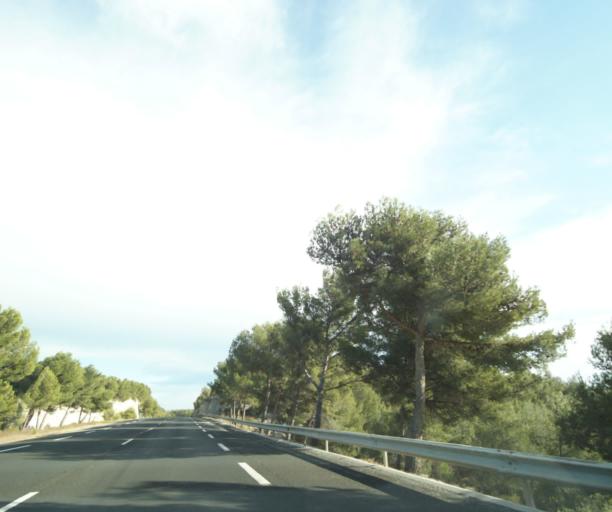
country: FR
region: Provence-Alpes-Cote d'Azur
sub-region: Departement des Bouches-du-Rhone
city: Sausset-les-Pins
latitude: 43.3457
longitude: 5.0730
